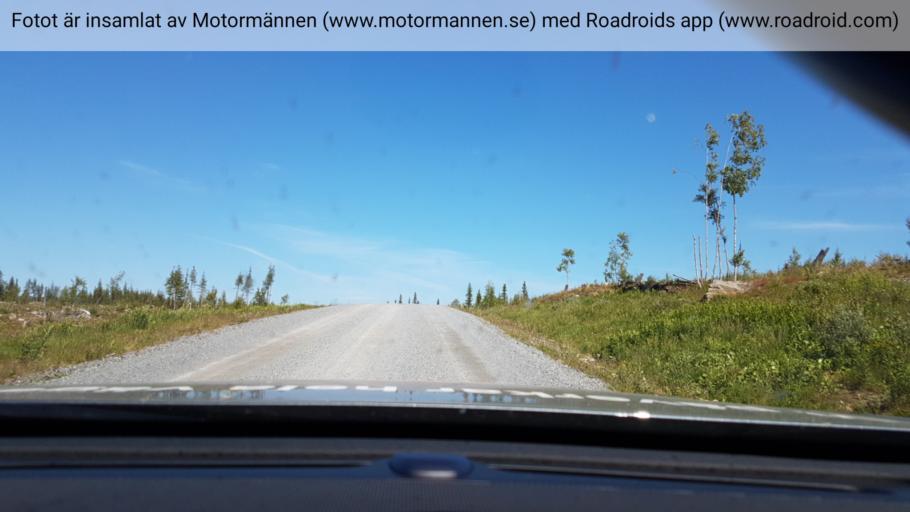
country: SE
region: Vaesterbotten
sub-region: Vilhelmina Kommun
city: Sjoberg
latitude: 64.6902
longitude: 15.7557
